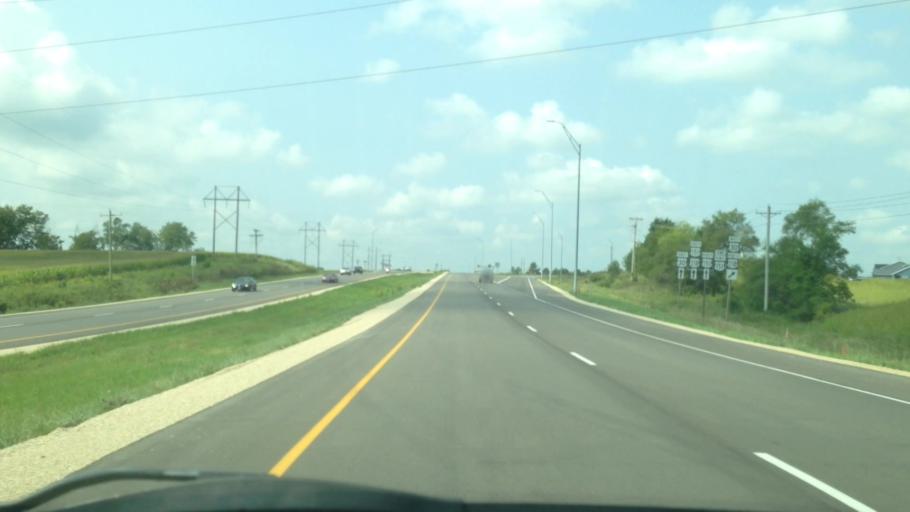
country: US
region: Iowa
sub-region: Linn County
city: Fairfax
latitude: 41.9478
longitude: -91.7352
